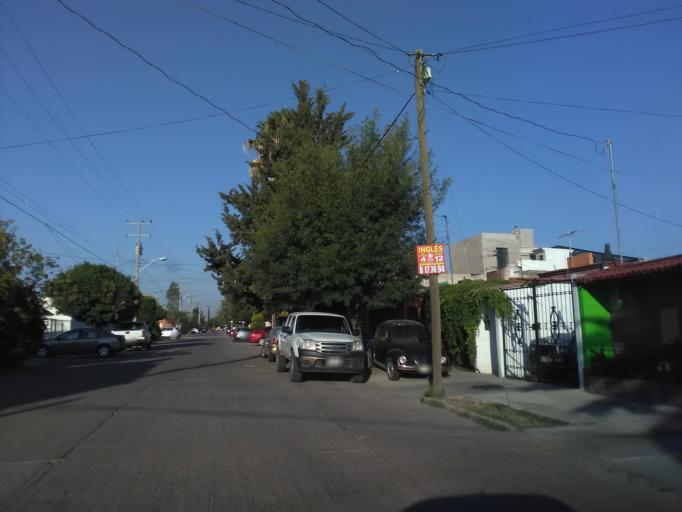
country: MX
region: Durango
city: Victoria de Durango
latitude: 24.0563
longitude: -104.6231
